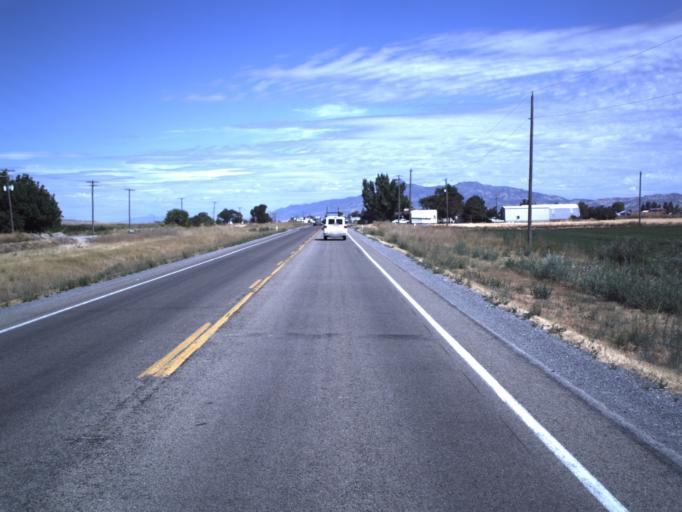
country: US
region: Utah
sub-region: Box Elder County
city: Elwood
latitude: 41.7035
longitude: -112.1419
